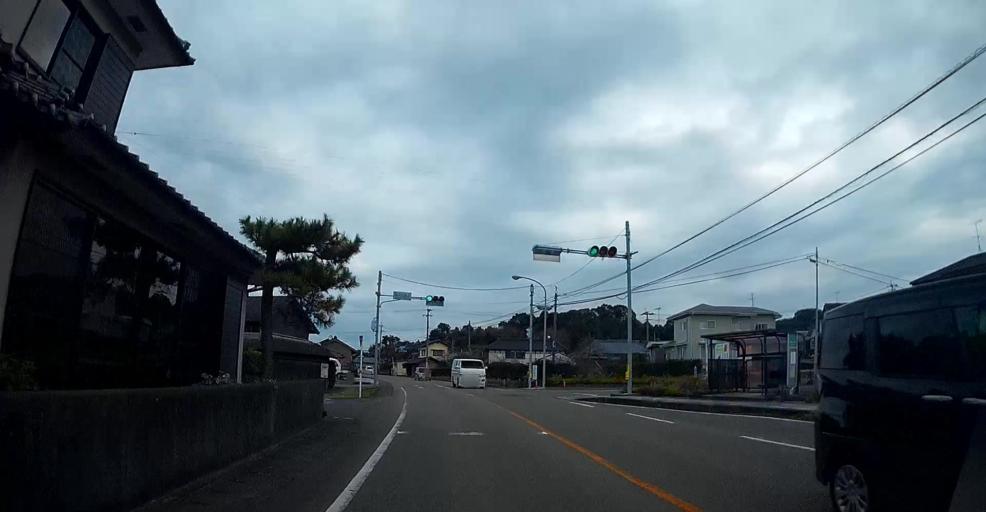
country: JP
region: Kumamoto
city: Hondo
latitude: 32.4739
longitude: 130.2594
